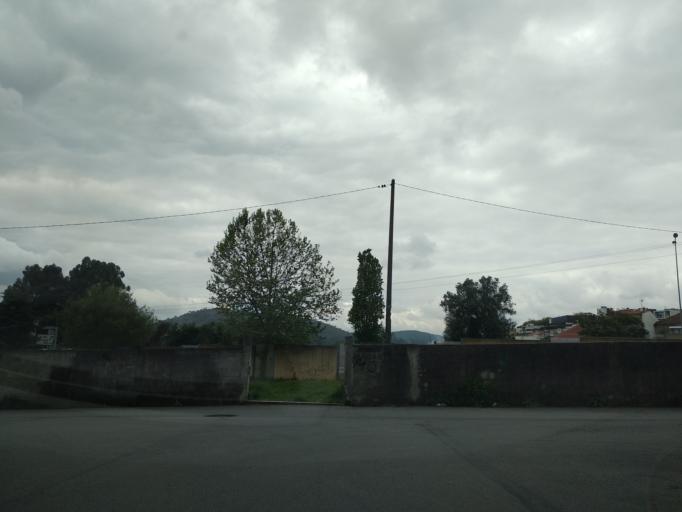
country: PT
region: Braga
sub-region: Braga
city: Braga
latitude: 41.5391
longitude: -8.4422
